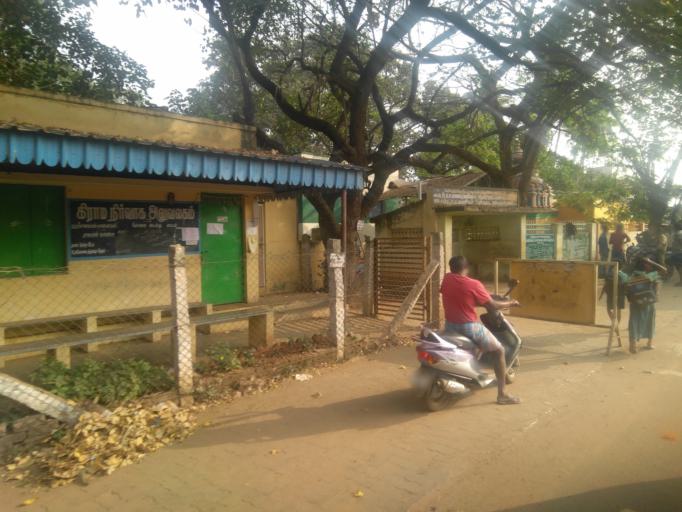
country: IN
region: Tamil Nadu
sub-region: Coimbatore
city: Coimbatore
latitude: 11.0562
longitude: 76.9038
